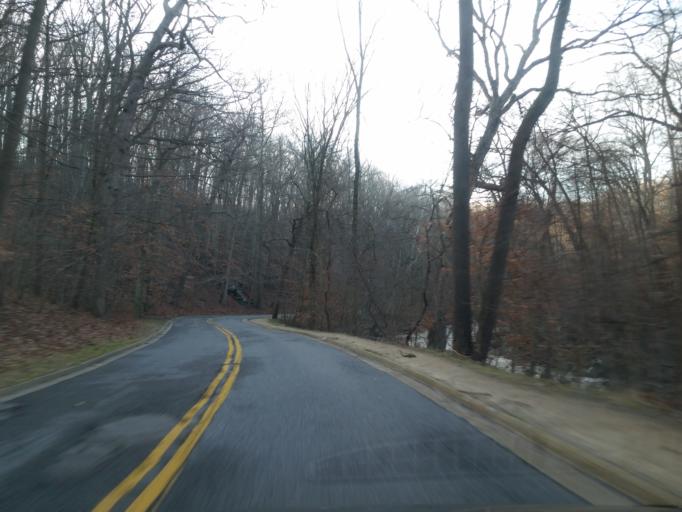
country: US
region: Maryland
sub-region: Montgomery County
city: Chevy Chase
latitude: 38.9519
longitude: -77.0445
